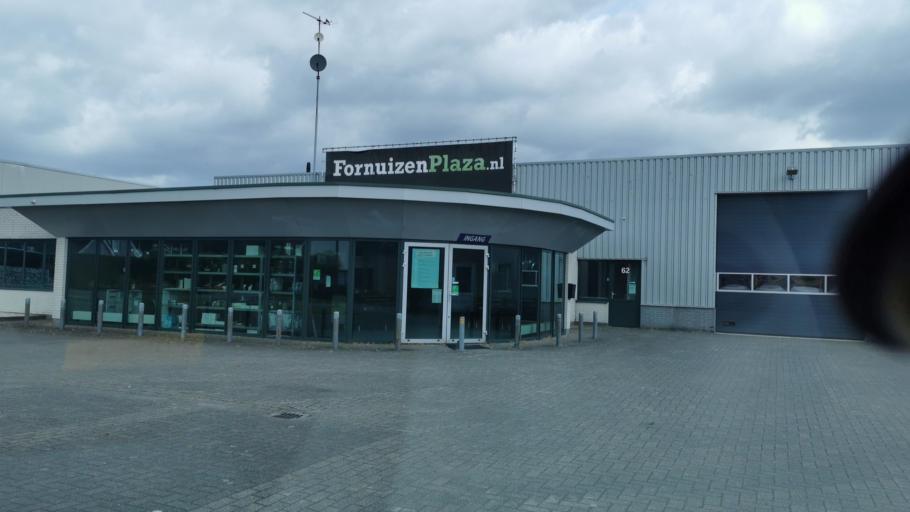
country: NL
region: Overijssel
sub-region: Gemeente Enschede
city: Enschede
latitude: 52.2247
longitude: 6.9557
